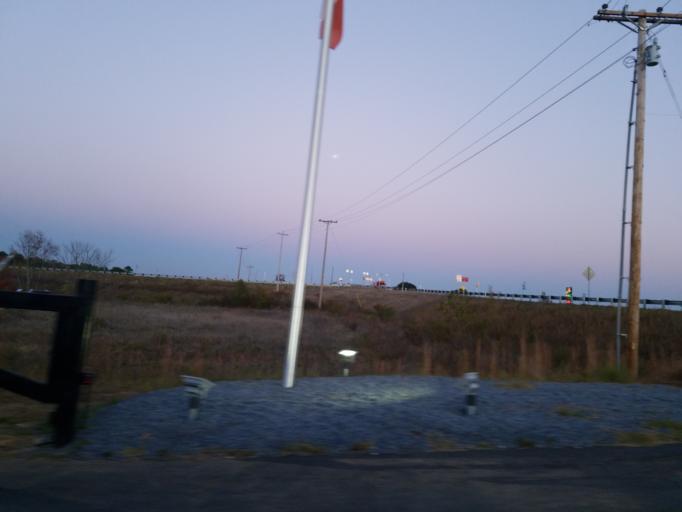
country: US
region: Georgia
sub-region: Gordon County
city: Calhoun
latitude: 34.5768
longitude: -84.9535
